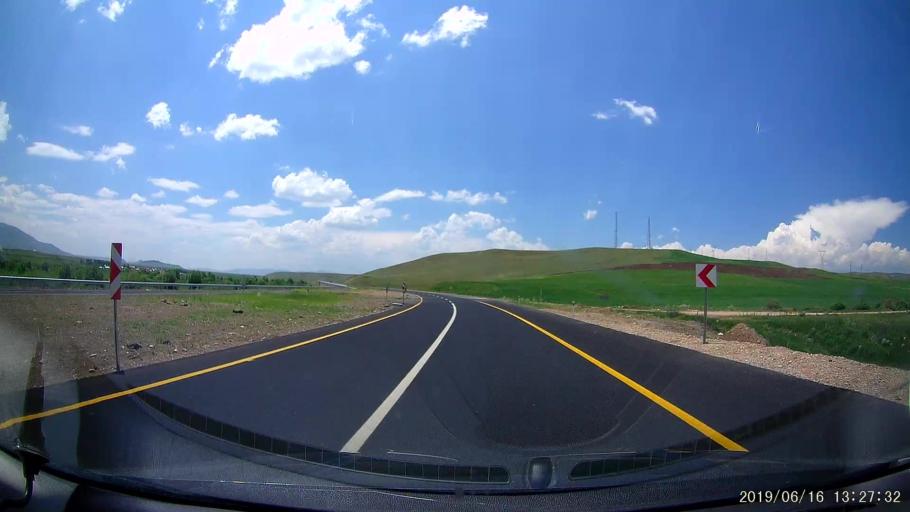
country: TR
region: Agri
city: Murat
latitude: 39.6716
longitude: 43.3083
